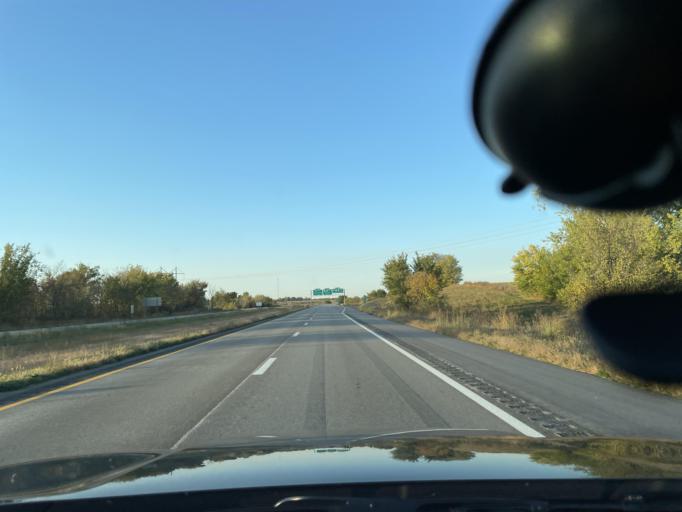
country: US
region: Missouri
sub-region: Andrew County
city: Country Club Village
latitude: 39.8761
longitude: -94.8571
